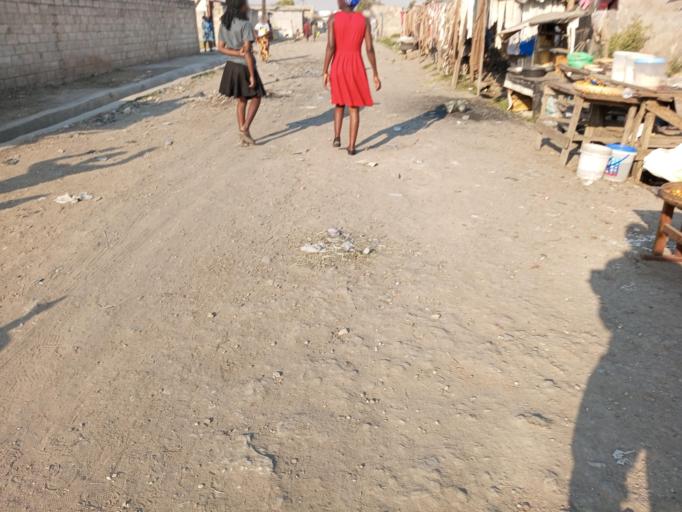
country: ZM
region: Lusaka
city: Lusaka
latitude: -15.3899
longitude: 28.2893
